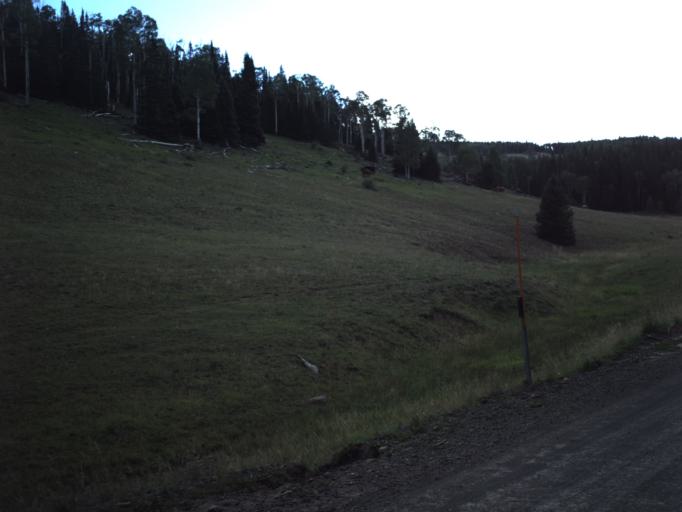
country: US
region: Utah
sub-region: Piute County
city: Junction
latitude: 38.2380
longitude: -112.3665
